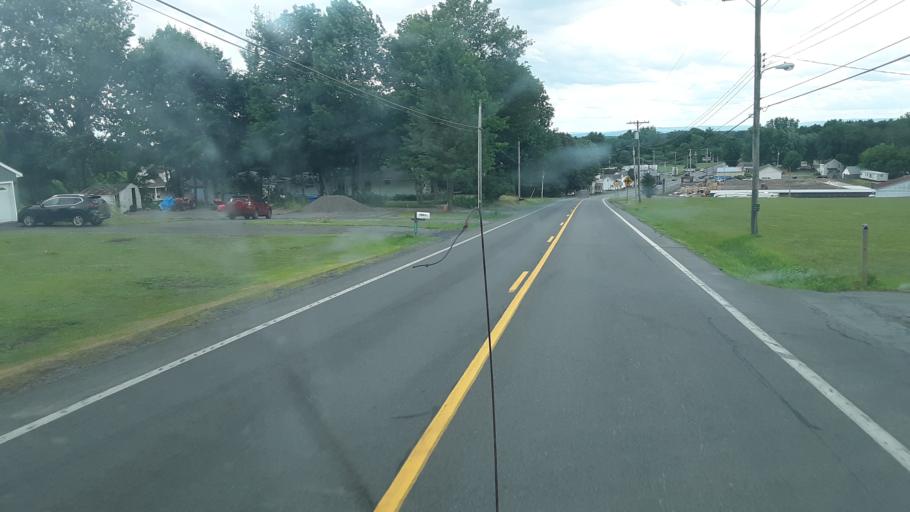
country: US
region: New York
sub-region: Oneida County
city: Rome
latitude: 43.3068
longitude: -75.4734
